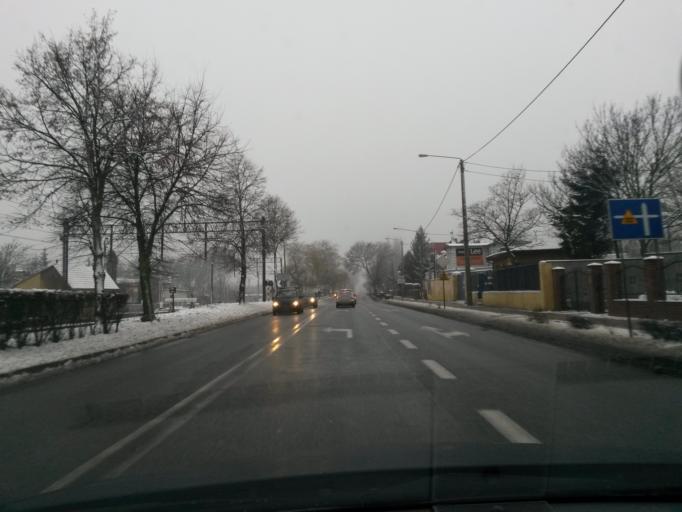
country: PL
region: Kujawsko-Pomorskie
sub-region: Powiat nakielski
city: Naklo nad Notecia
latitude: 53.1406
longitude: 17.5981
